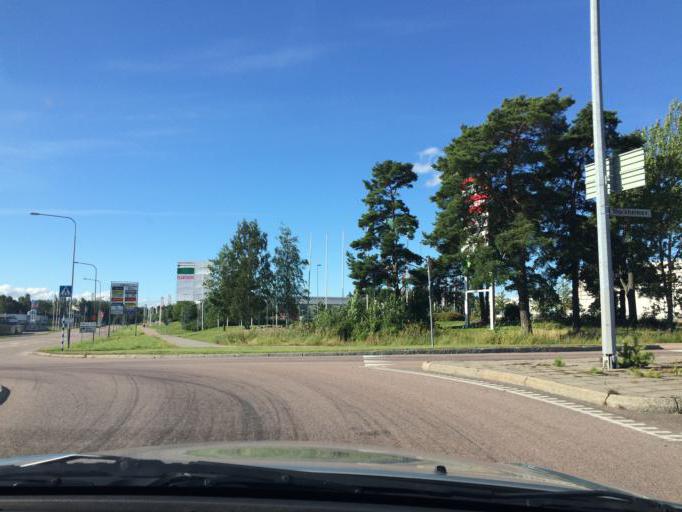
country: SE
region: Vaestmanland
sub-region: Vasteras
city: Vasteras
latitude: 59.6124
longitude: 16.6139
